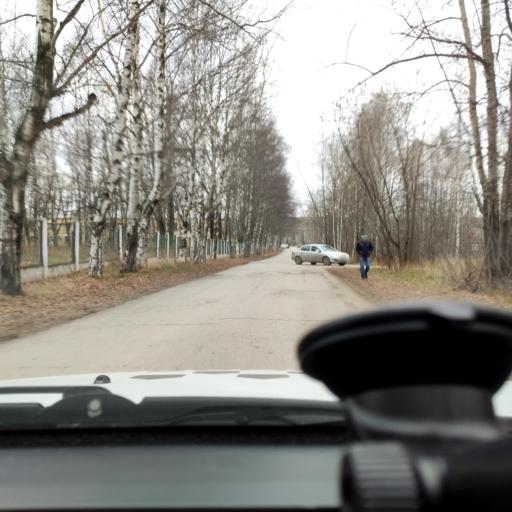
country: RU
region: Perm
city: Perm
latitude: 58.1186
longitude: 56.3724
